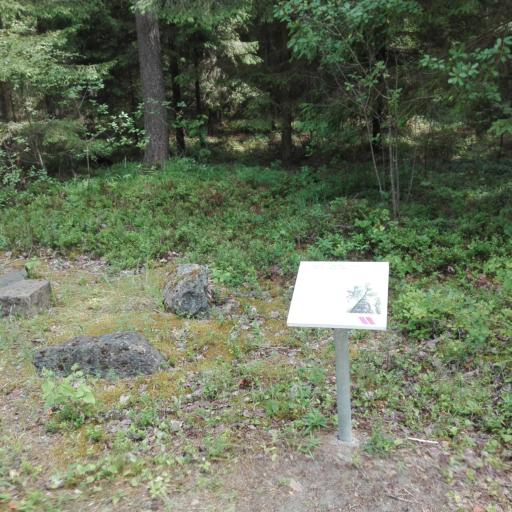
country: LT
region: Panevezys
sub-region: Birzai
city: Birzai
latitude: 56.2671
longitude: 24.7531
